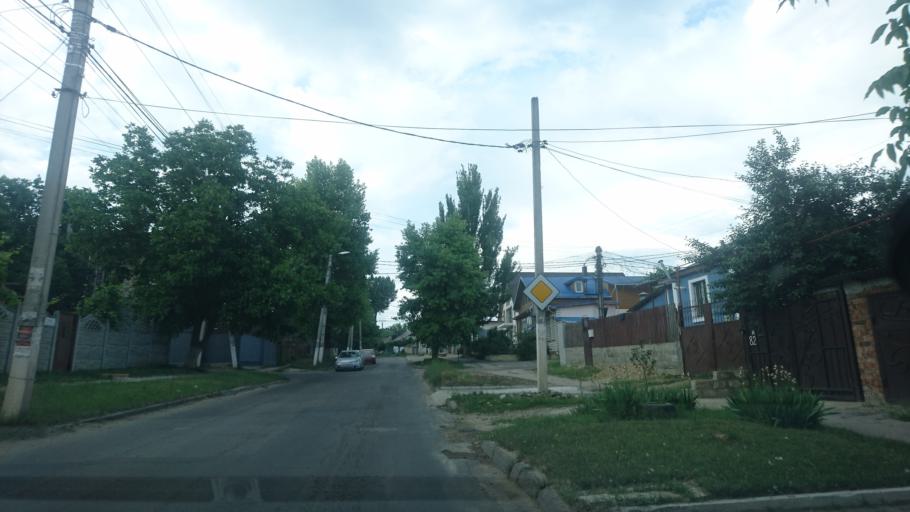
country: MD
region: Chisinau
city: Chisinau
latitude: 47.0528
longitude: 28.8421
